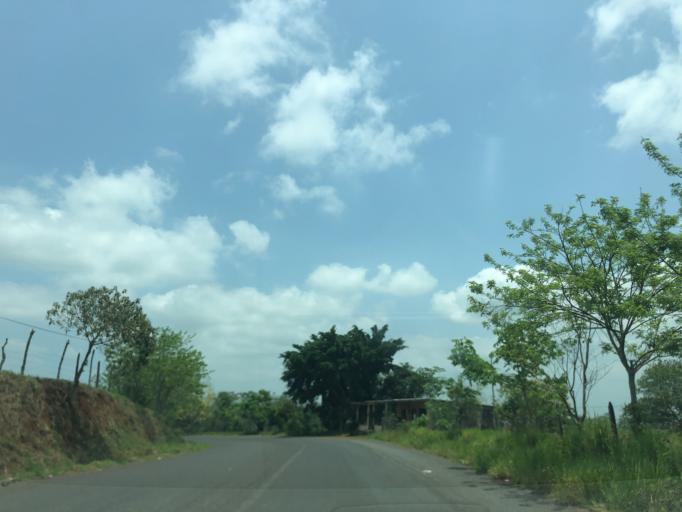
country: MX
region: Chiapas
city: Pueblo Juarez
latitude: 17.6020
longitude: -93.1817
